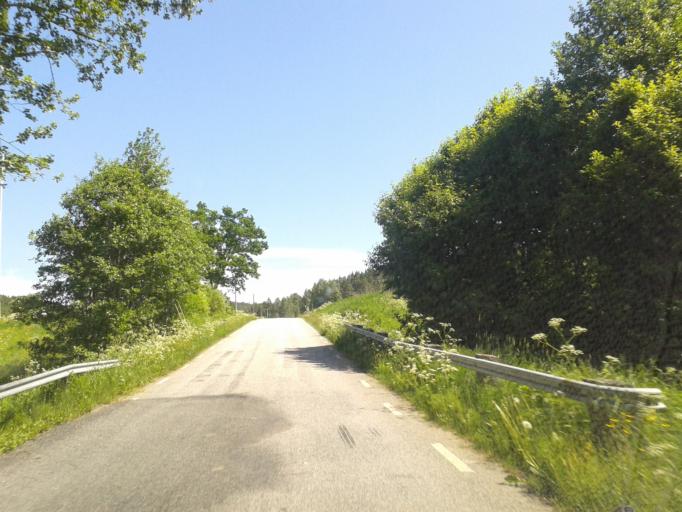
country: SE
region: Vaestra Goetaland
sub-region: Stromstads Kommun
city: Stroemstad
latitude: 58.8948
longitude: 11.3098
